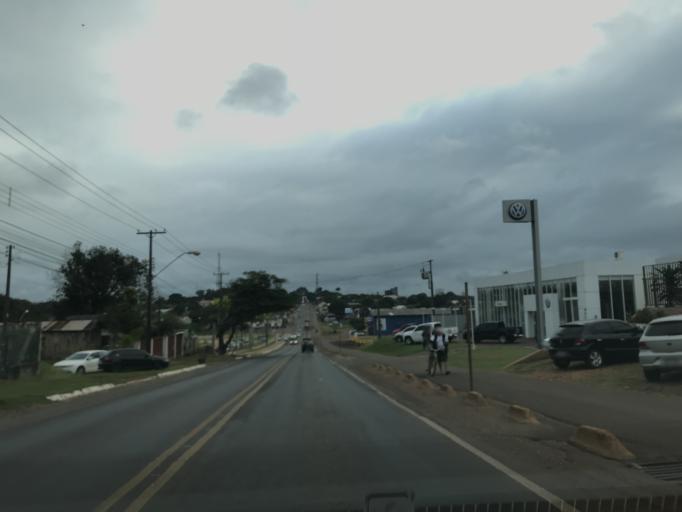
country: PY
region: Canindeyu
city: Salto del Guaira
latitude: -24.0895
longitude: -54.2408
